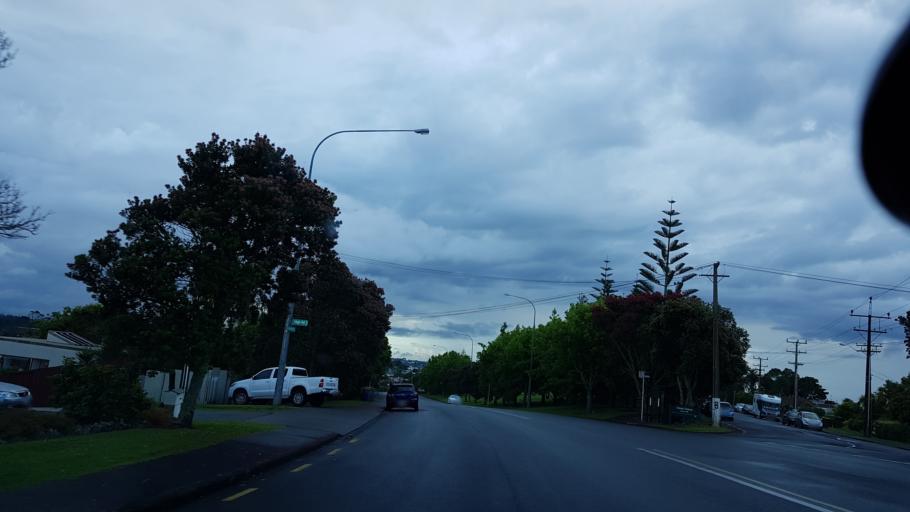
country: NZ
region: Auckland
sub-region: Auckland
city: North Shore
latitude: -36.7883
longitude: 174.7213
